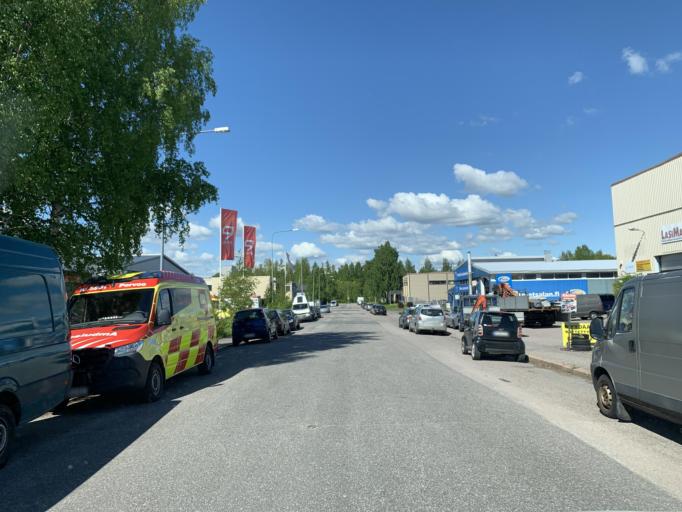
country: FI
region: Uusimaa
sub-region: Helsinki
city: Vantaa
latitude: 60.2542
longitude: 25.0265
